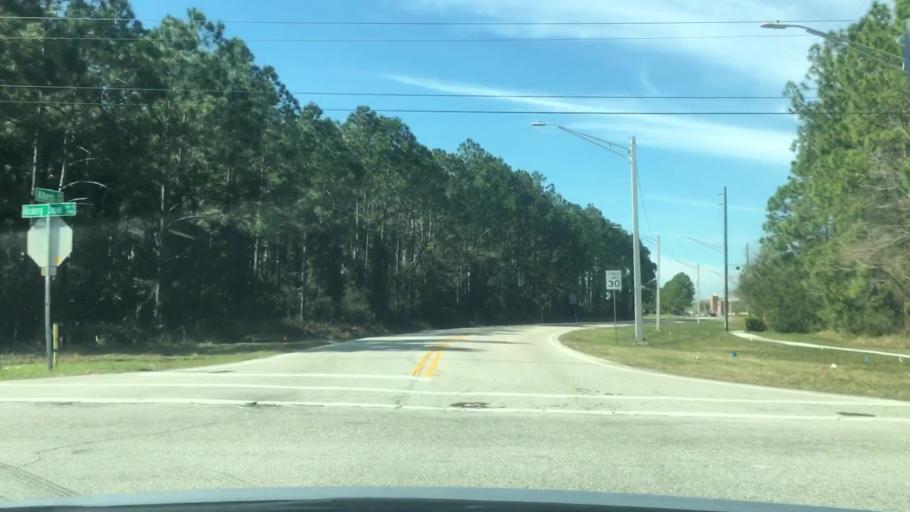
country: US
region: Florida
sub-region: Duval County
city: Atlantic Beach
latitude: 30.3216
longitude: -81.4818
